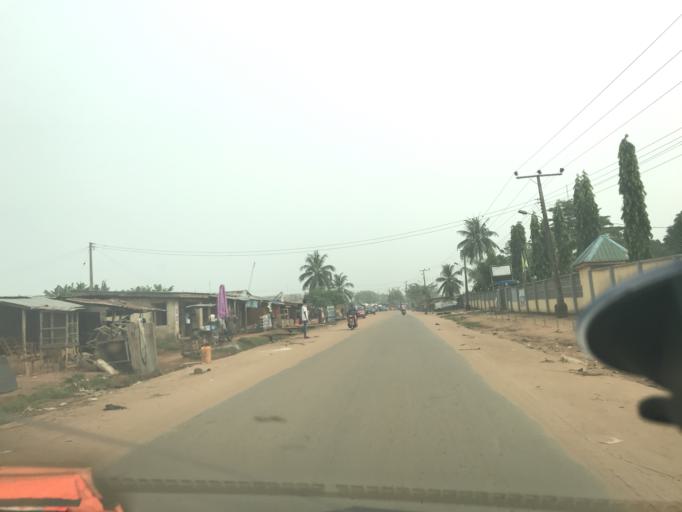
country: NG
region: Ogun
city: Ado Odo
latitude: 6.5082
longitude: 2.9537
